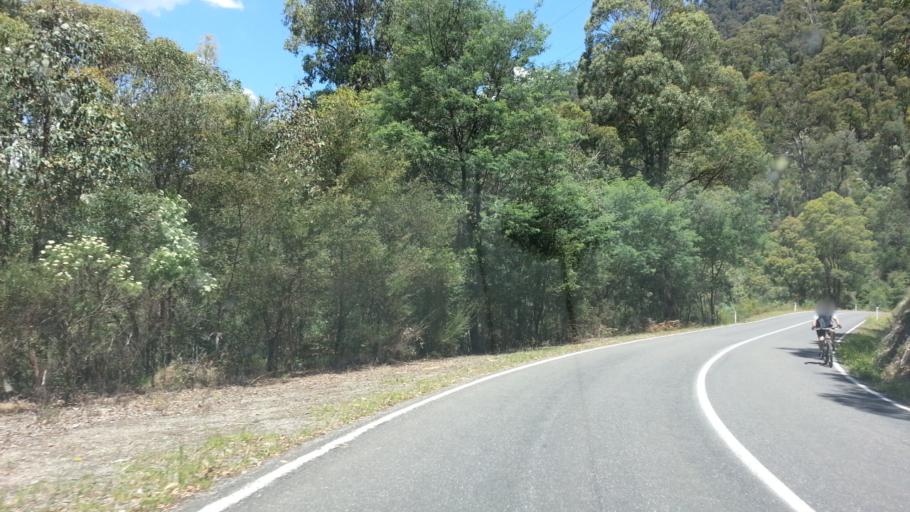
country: AU
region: Victoria
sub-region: Alpine
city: Mount Beauty
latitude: -36.7598
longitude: 147.2072
